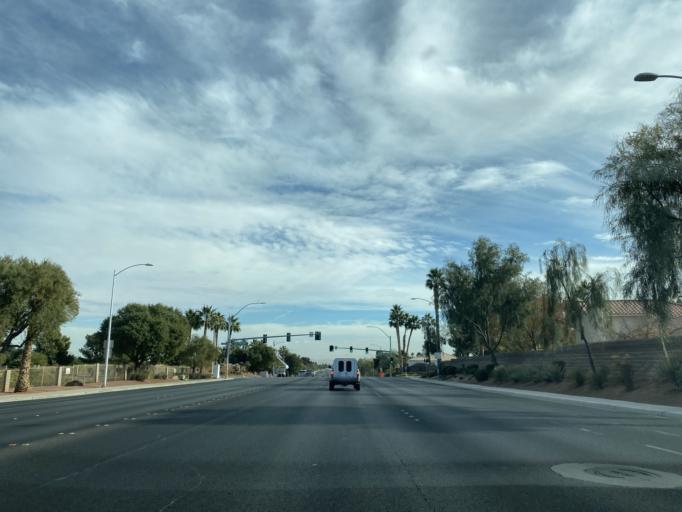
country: US
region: Nevada
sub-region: Clark County
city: Las Vegas
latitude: 36.2464
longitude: -115.2189
